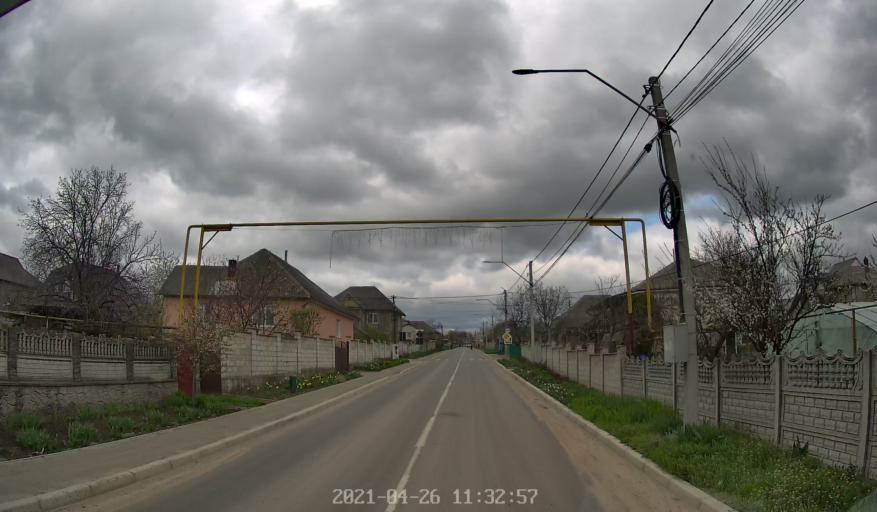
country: MD
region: Chisinau
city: Ciorescu
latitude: 47.1307
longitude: 28.9000
